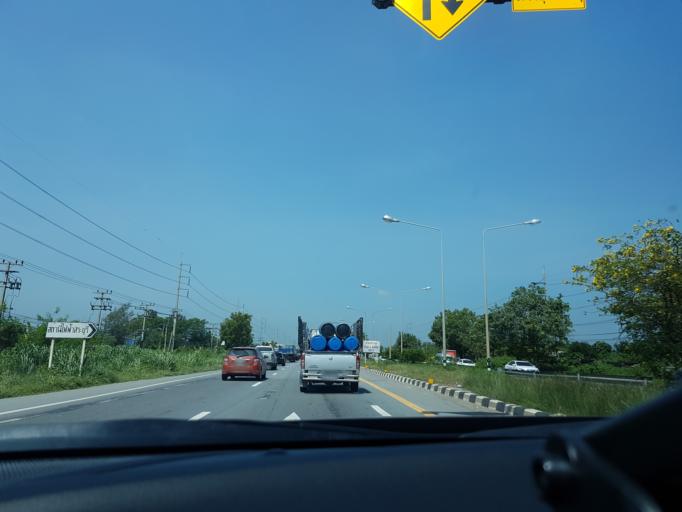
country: TH
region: Sara Buri
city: Saraburi
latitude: 14.5155
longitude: 100.8970
